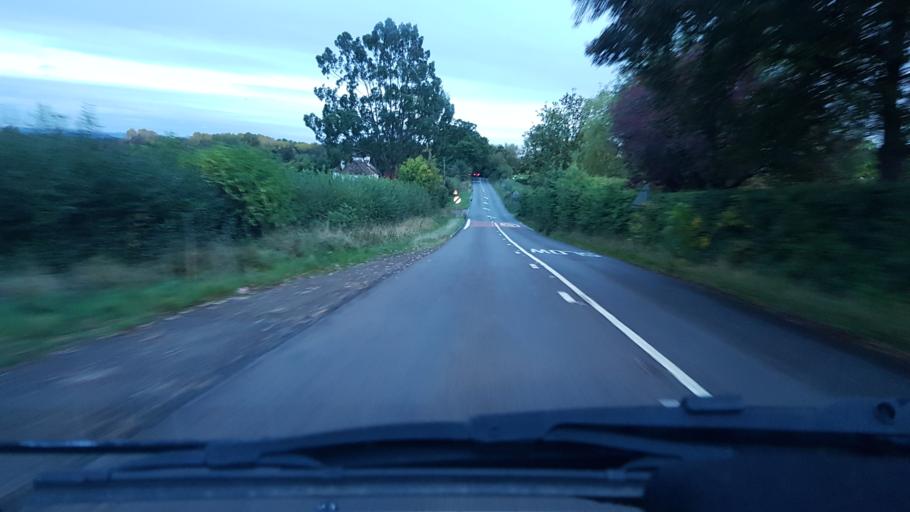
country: GB
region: England
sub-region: Worcestershire
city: Great Malvern
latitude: 52.0943
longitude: -2.3116
